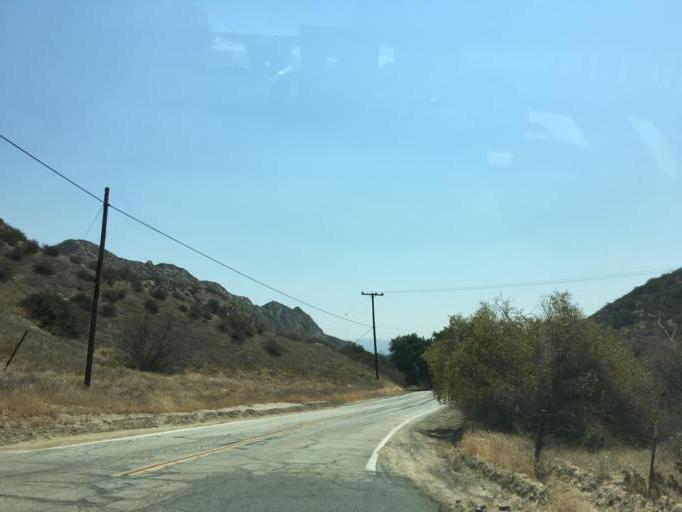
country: US
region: California
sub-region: Los Angeles County
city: Valencia
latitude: 34.3810
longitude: -118.6046
